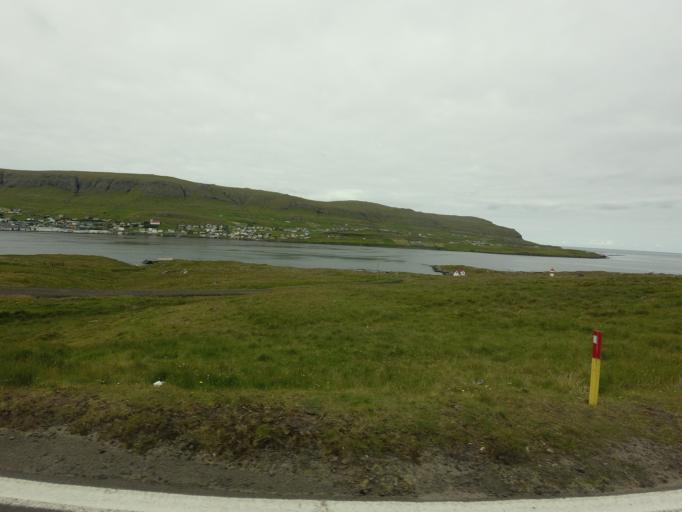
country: FO
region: Suduroy
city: Tvoroyri
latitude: 61.5428
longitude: -6.8077
